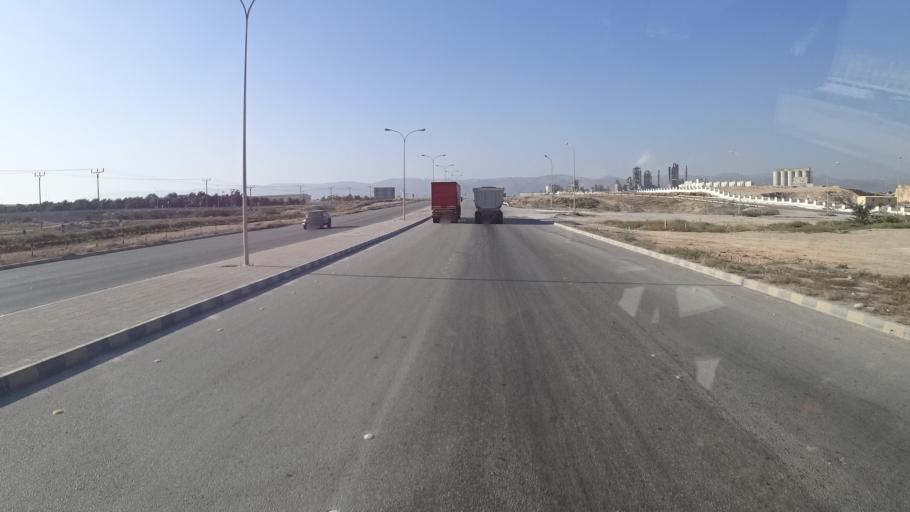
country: OM
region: Zufar
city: Salalah
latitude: 16.9654
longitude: 53.9935
